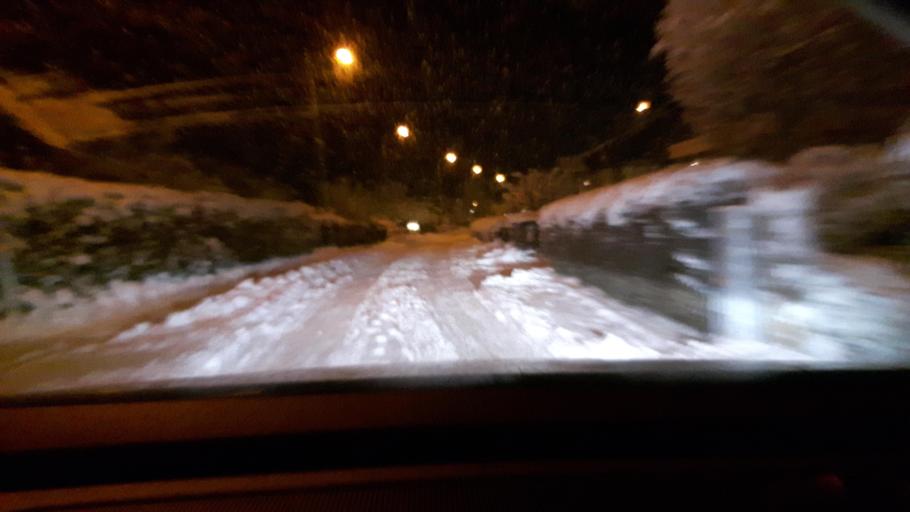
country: SE
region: Vaestra Goetaland
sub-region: Goteborg
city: Majorna
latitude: 57.6627
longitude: 11.8807
